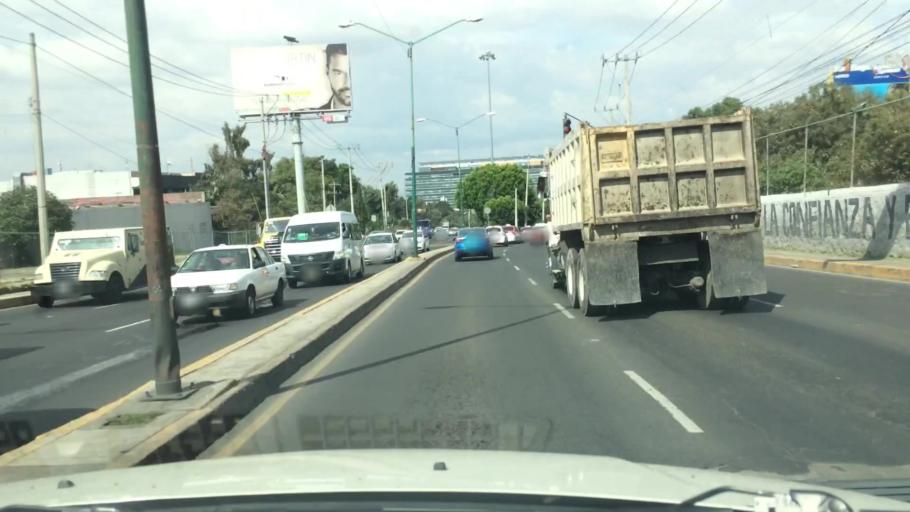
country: MX
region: Mexico City
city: Magdalena Contreras
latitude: 19.2947
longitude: -99.2152
